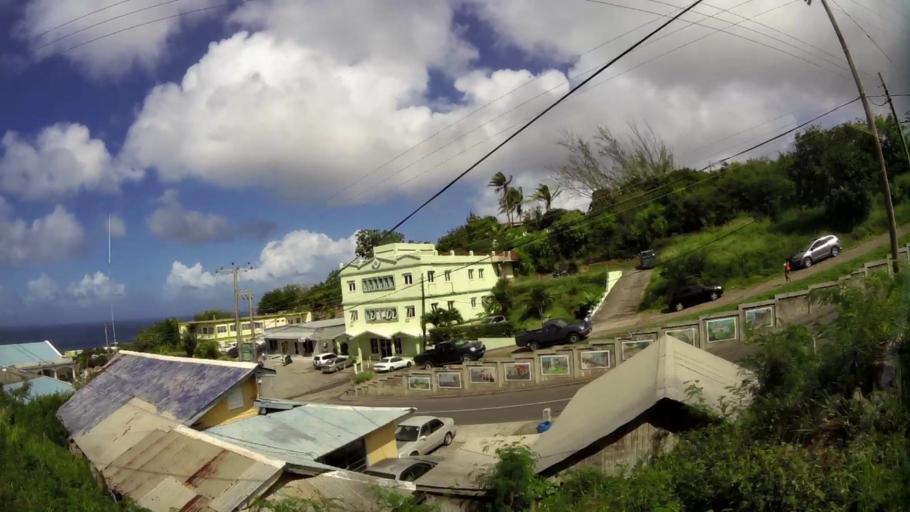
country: MS
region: Saint Peter
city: Brades
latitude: 16.7856
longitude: -62.2085
